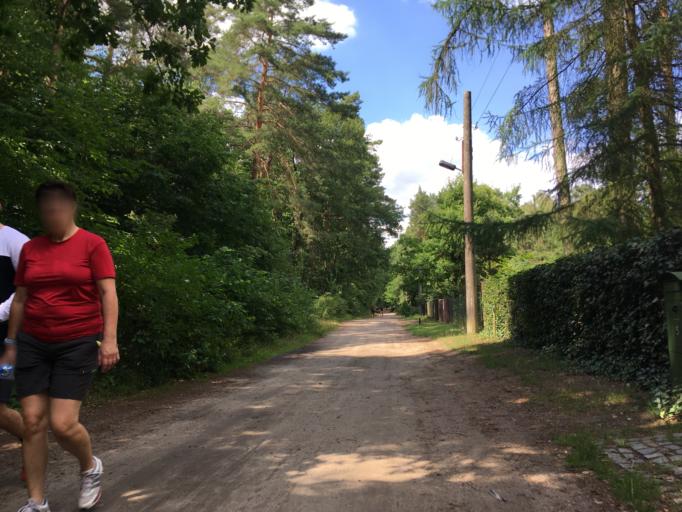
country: DE
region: Brandenburg
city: Wandlitz
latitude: 52.7488
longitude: 13.4874
